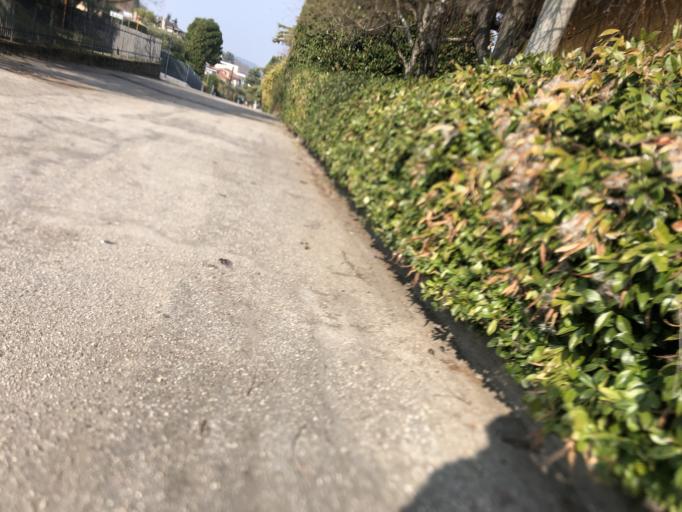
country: IT
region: Veneto
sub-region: Provincia di Verona
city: Sona
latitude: 45.4311
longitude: 10.8384
